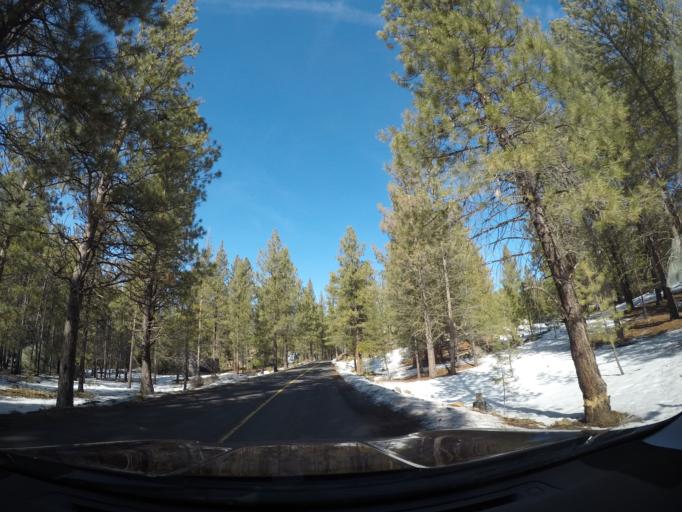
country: US
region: Oregon
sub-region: Deschutes County
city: Sunriver
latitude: 43.8746
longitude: -121.4313
